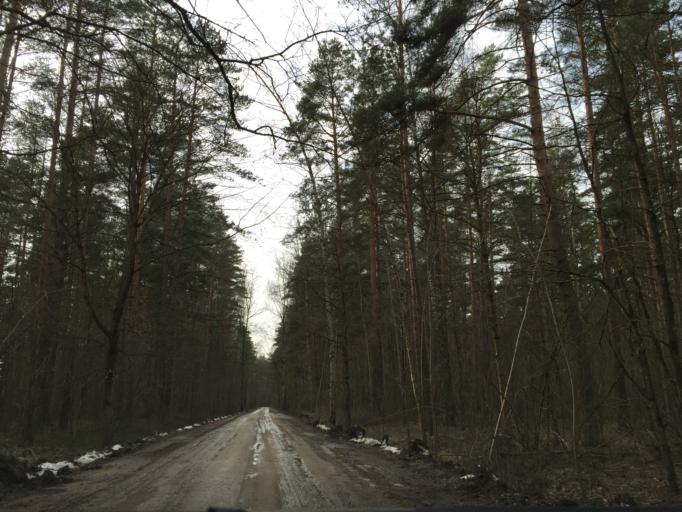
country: LV
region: Stopini
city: Ulbroka
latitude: 56.9221
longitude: 24.2988
